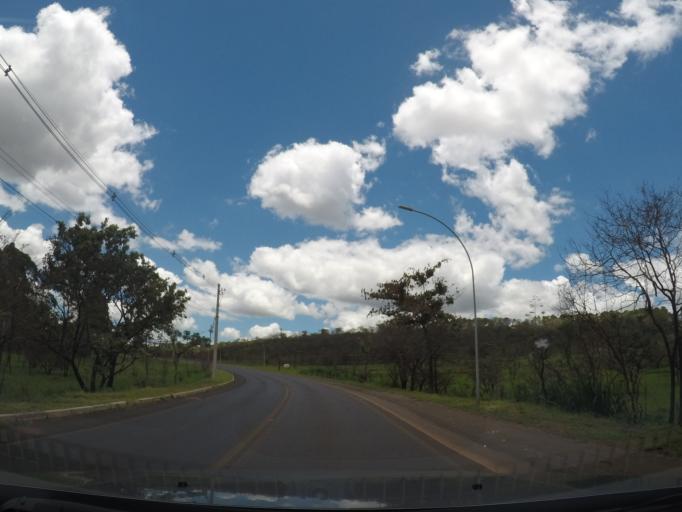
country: BR
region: Federal District
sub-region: Brasilia
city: Brasilia
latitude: -15.7645
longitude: -47.8085
